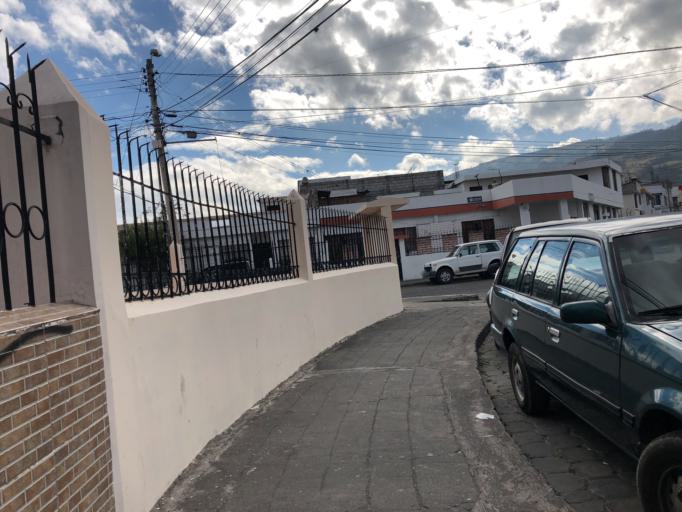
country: EC
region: Imbabura
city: Ibarra
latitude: 0.3500
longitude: -78.1248
